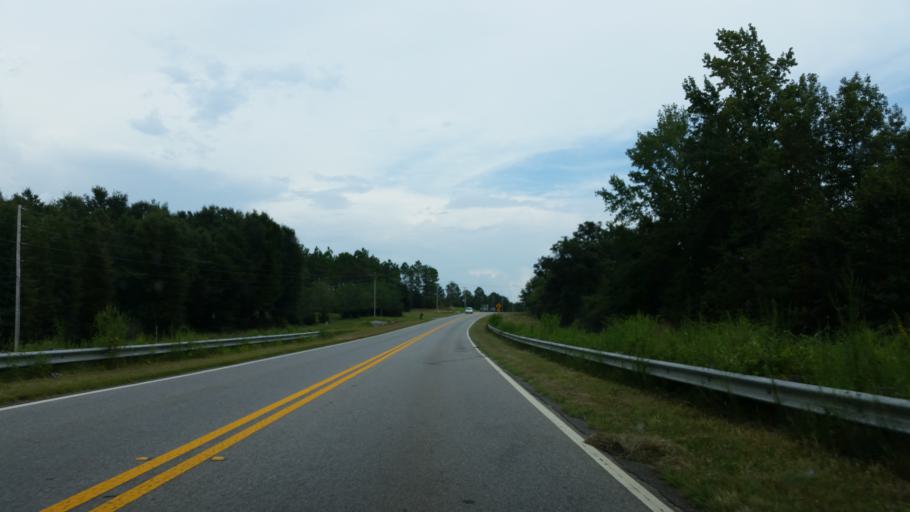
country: US
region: Florida
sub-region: Santa Rosa County
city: Wallace
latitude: 30.6723
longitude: -87.2216
